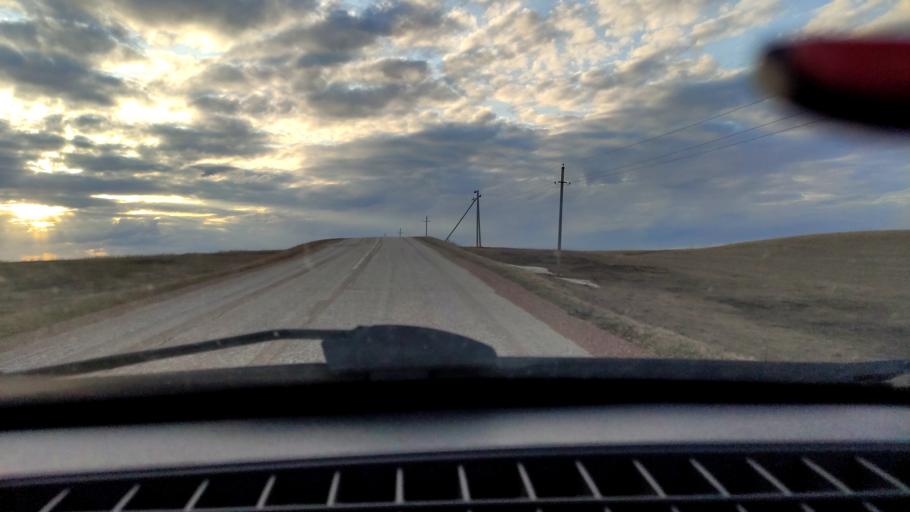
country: RU
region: Bashkortostan
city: Tolbazy
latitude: 54.0027
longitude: 55.6526
